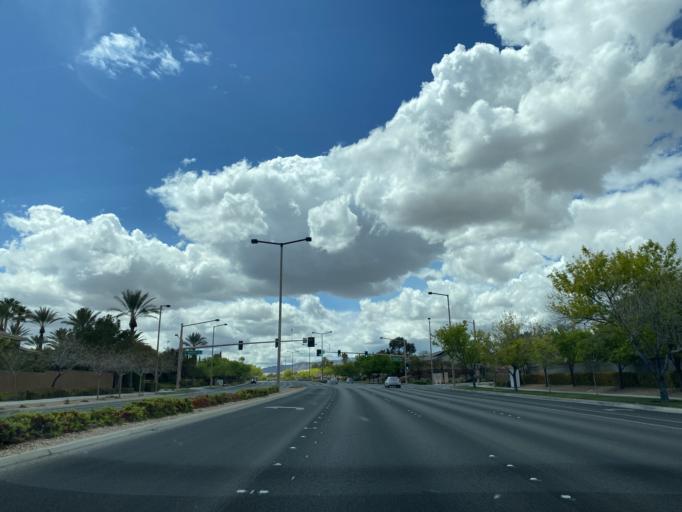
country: US
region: Nevada
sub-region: Clark County
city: Summerlin South
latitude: 36.1756
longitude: -115.3221
